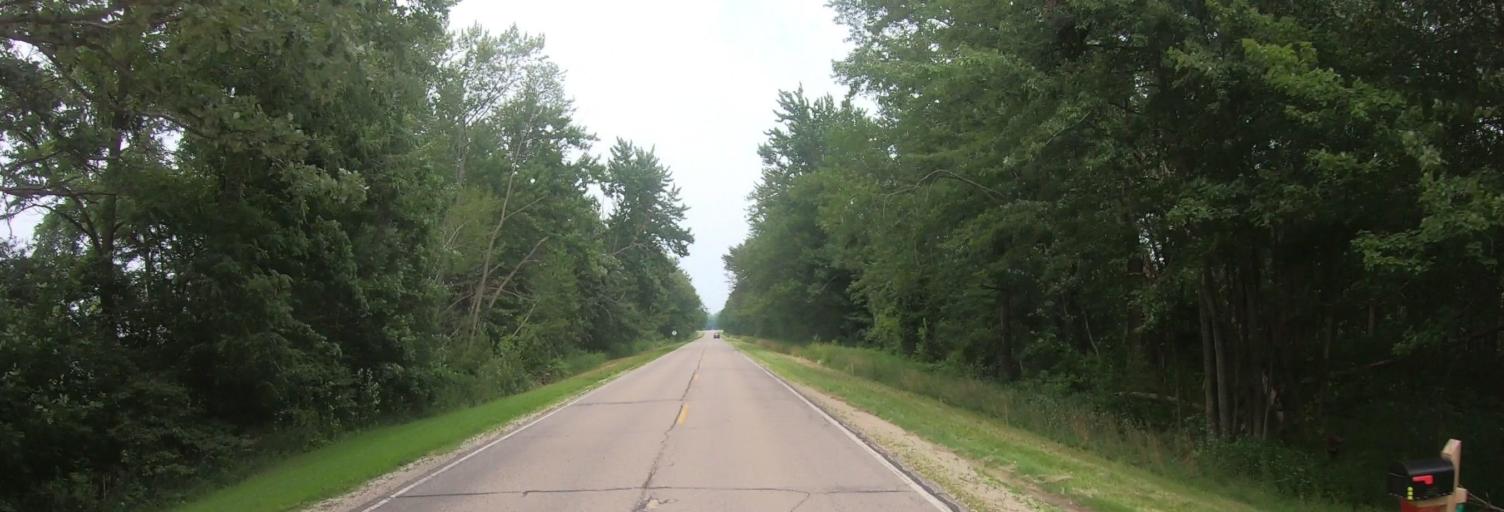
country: US
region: Michigan
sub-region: Shiawassee County
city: Perry
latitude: 42.8655
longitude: -84.1150
